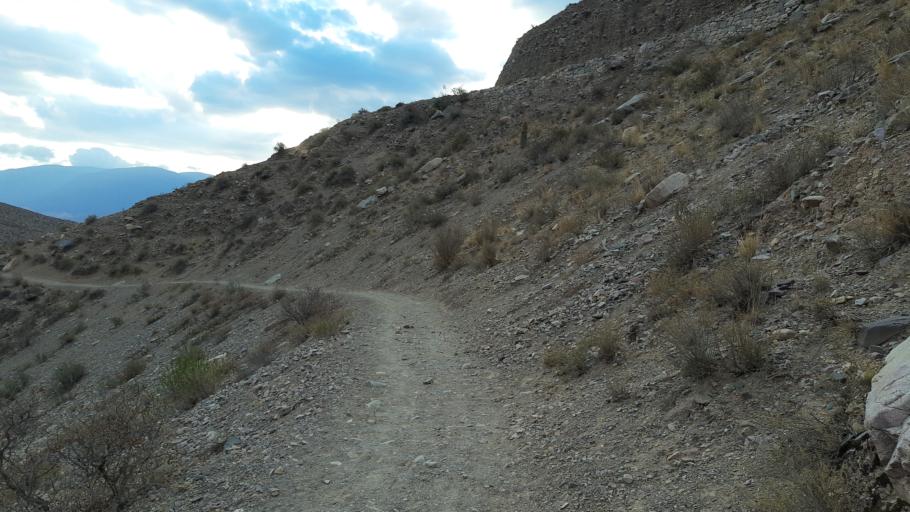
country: AR
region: Jujuy
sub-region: Departamento de Tilcara
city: Tilcara
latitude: -23.5927
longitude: -65.3797
